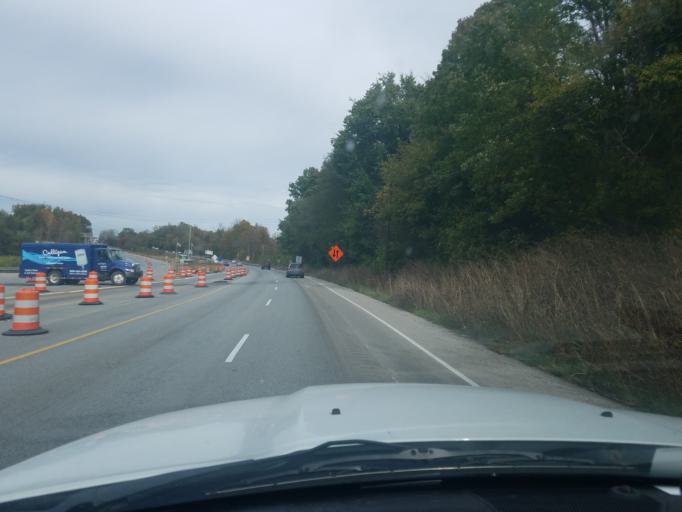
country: US
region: Kentucky
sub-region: Henderson County
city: Henderson
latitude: 37.8879
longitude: -87.5579
